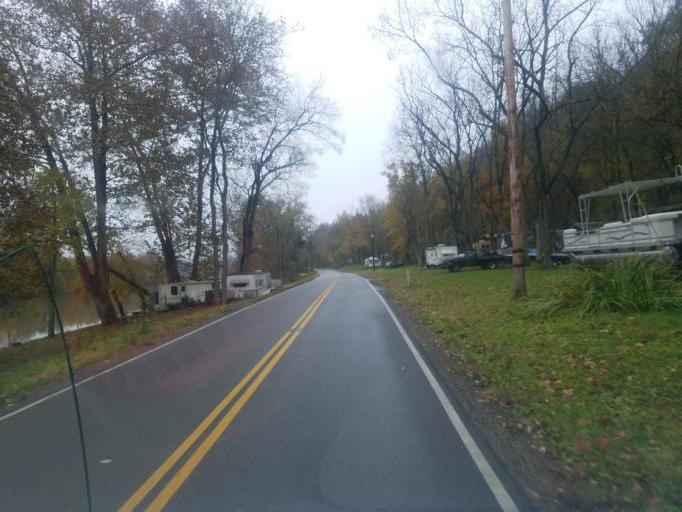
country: US
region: Ohio
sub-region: Morgan County
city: McConnelsville
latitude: 39.6123
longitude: -81.8317
